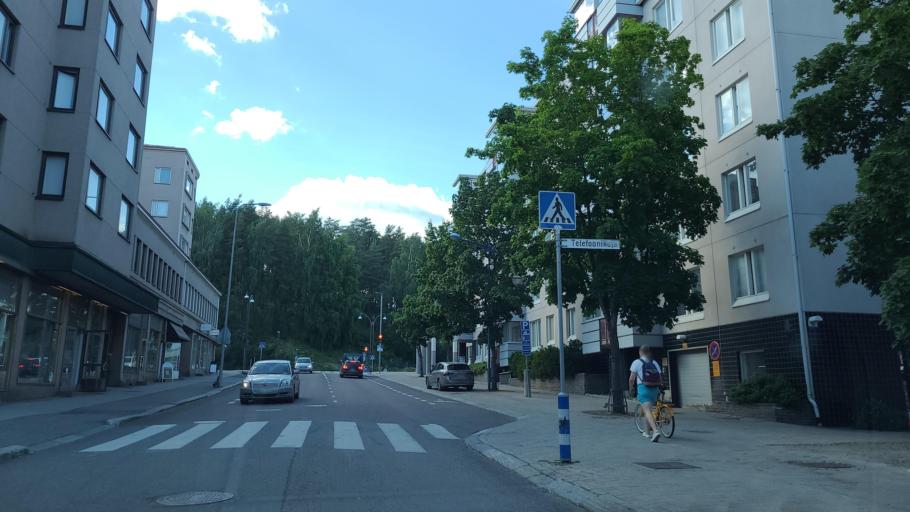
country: FI
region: Central Finland
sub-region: Jyvaeskylae
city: Jyvaeskylae
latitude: 62.2420
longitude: 25.7442
